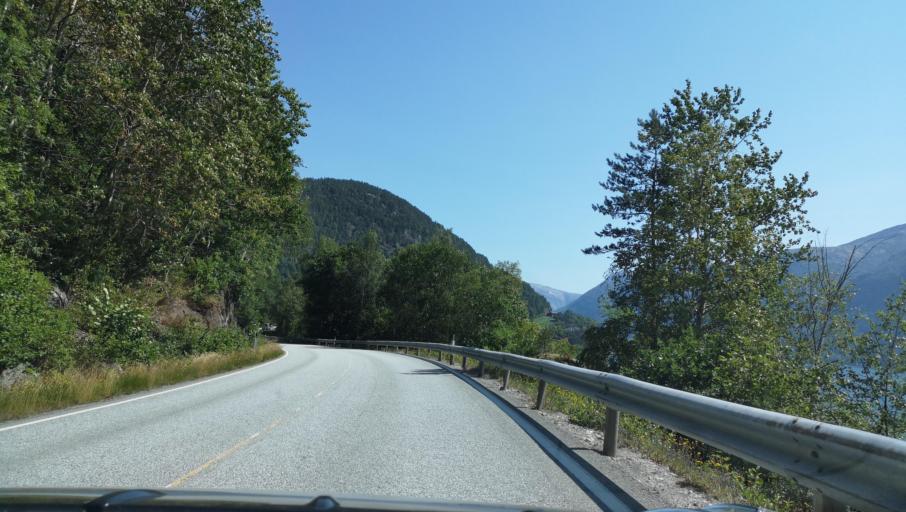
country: NO
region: Hordaland
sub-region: Ulvik
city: Ulvik
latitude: 60.4890
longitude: 6.8471
